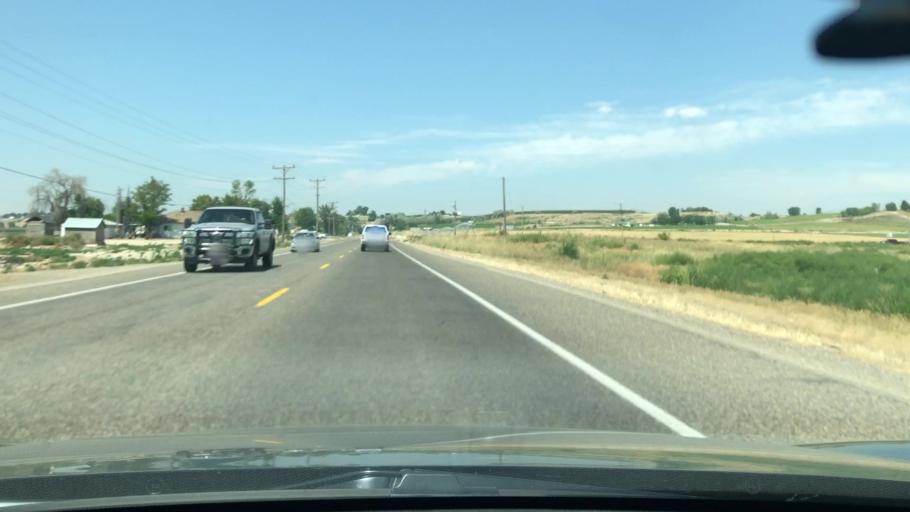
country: US
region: Idaho
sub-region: Canyon County
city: Wilder
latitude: 43.6450
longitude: -116.9117
